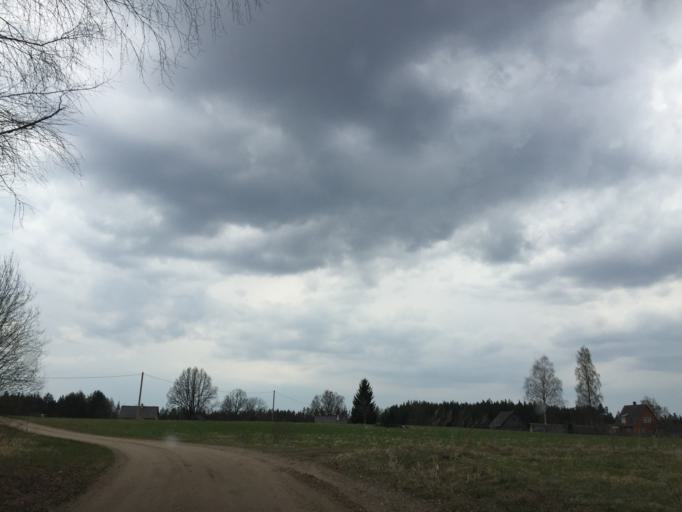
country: EE
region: Vorumaa
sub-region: Antsla vald
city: Vana-Antsla
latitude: 57.9468
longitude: 26.7169
